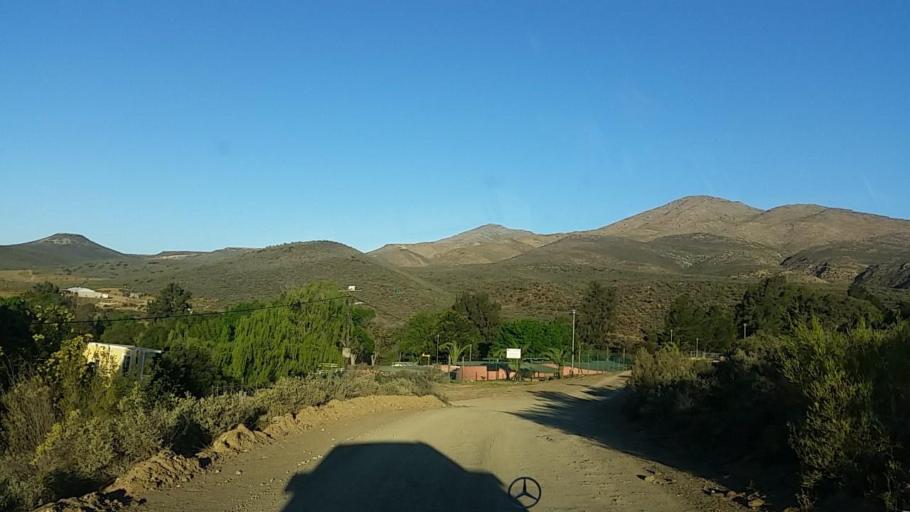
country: ZA
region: Western Cape
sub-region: Eden District Municipality
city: Knysna
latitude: -33.6564
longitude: 23.1364
